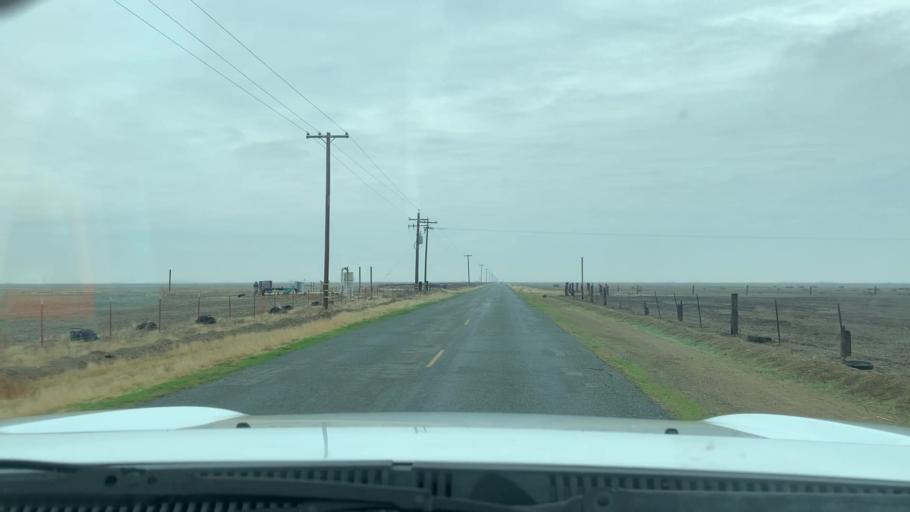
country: US
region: California
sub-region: Tulare County
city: Alpaugh
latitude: 35.7609
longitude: -119.5002
